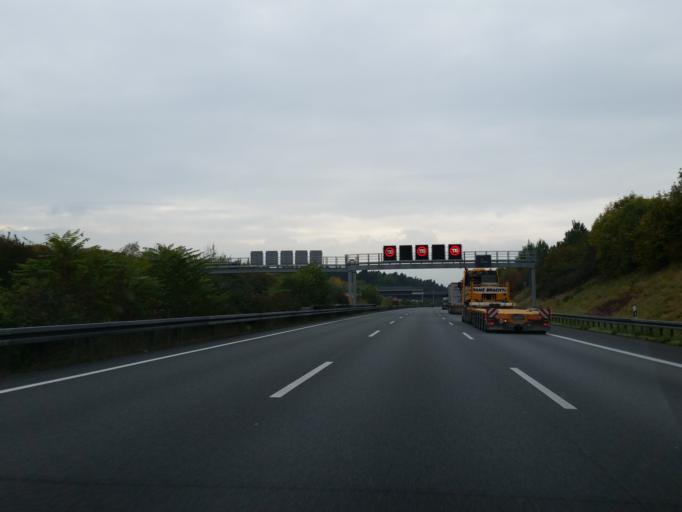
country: DE
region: Lower Saxony
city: Arpke
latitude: 52.3638
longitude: 10.1128
